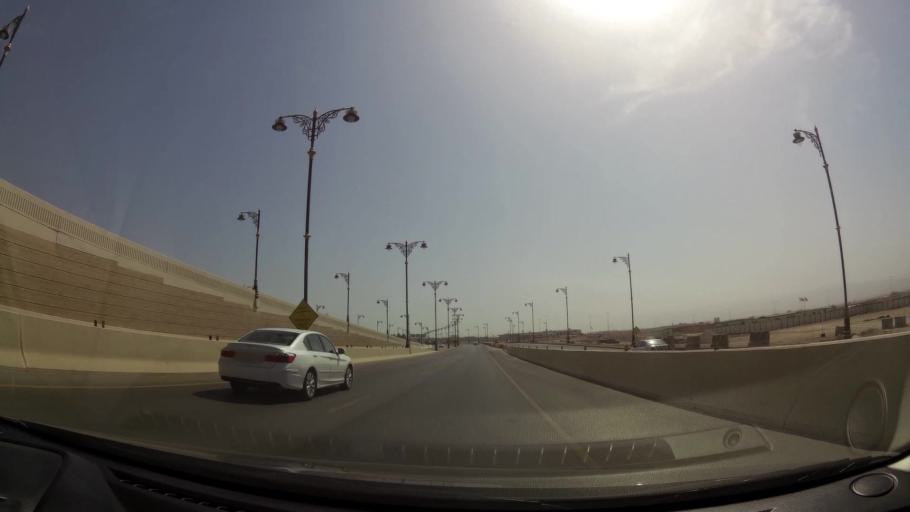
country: OM
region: Zufar
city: Salalah
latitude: 17.0310
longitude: 54.1389
